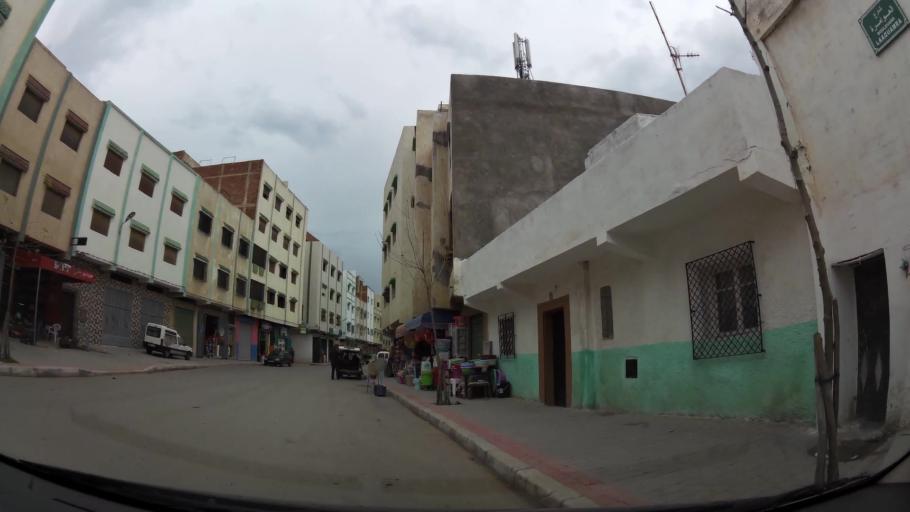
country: MA
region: Tanger-Tetouan
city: Tetouan
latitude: 35.5636
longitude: -5.3467
